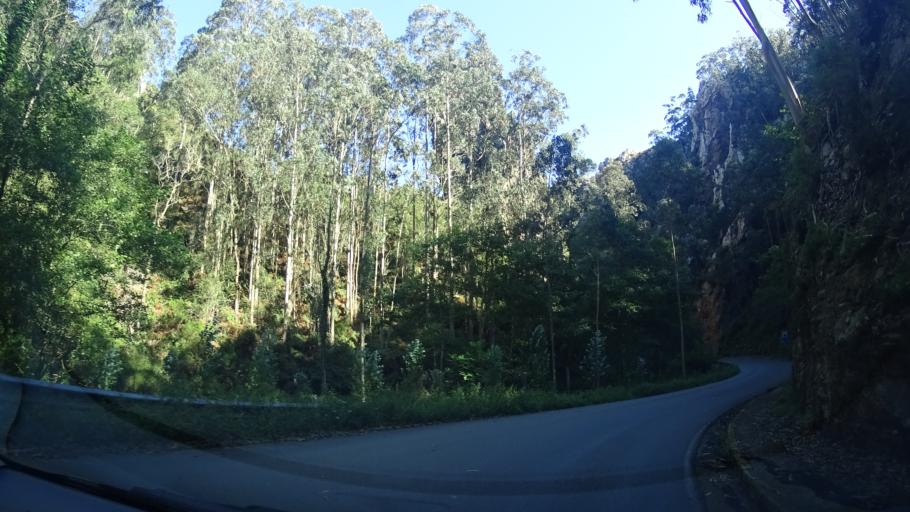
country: ES
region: Asturias
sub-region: Province of Asturias
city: Ribadesella
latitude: 43.4713
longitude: -5.1325
